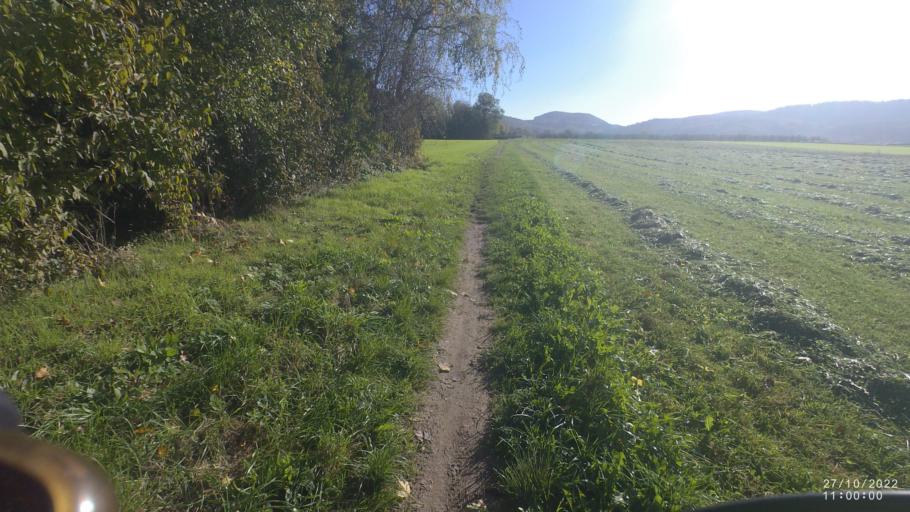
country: DE
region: Baden-Wuerttemberg
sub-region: Regierungsbezirk Stuttgart
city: Schlat
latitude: 48.6635
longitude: 9.6967
